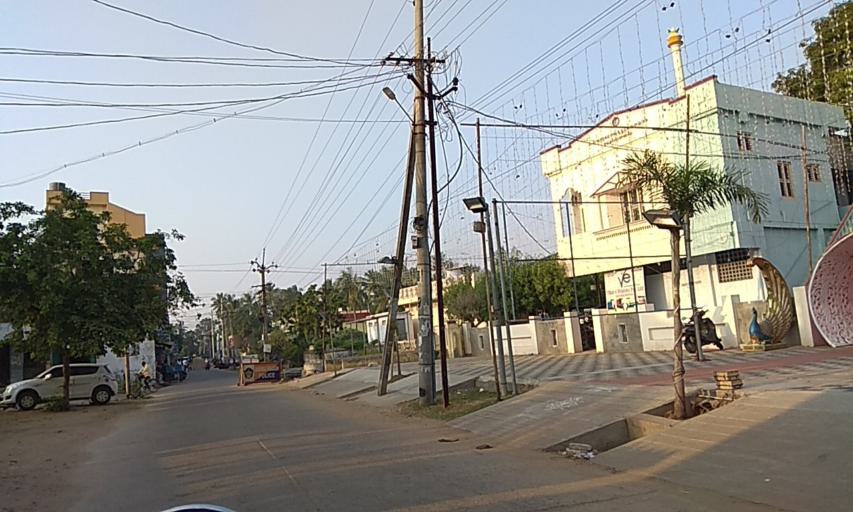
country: IN
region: Andhra Pradesh
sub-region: Krishna
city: Machilipatnam
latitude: 16.1873
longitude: 81.1347
